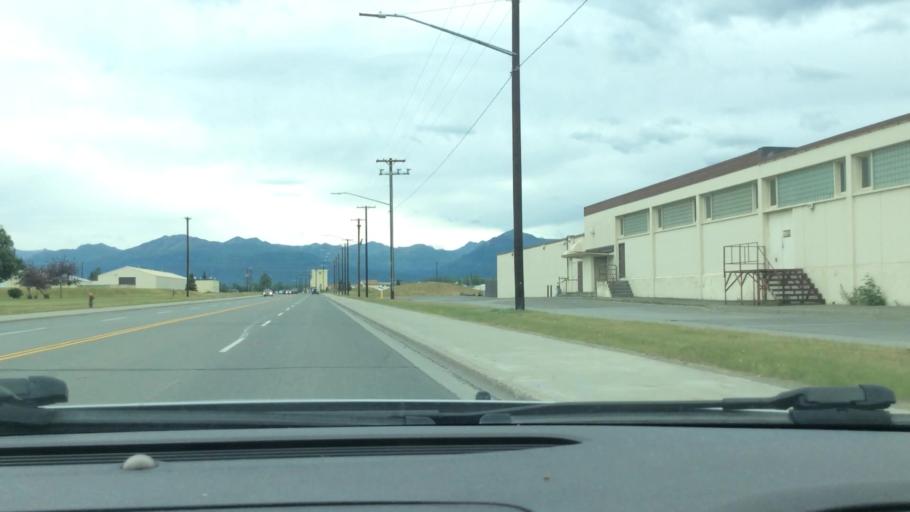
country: US
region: Alaska
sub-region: Anchorage Municipality
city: Anchorage
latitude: 61.2372
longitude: -149.8443
